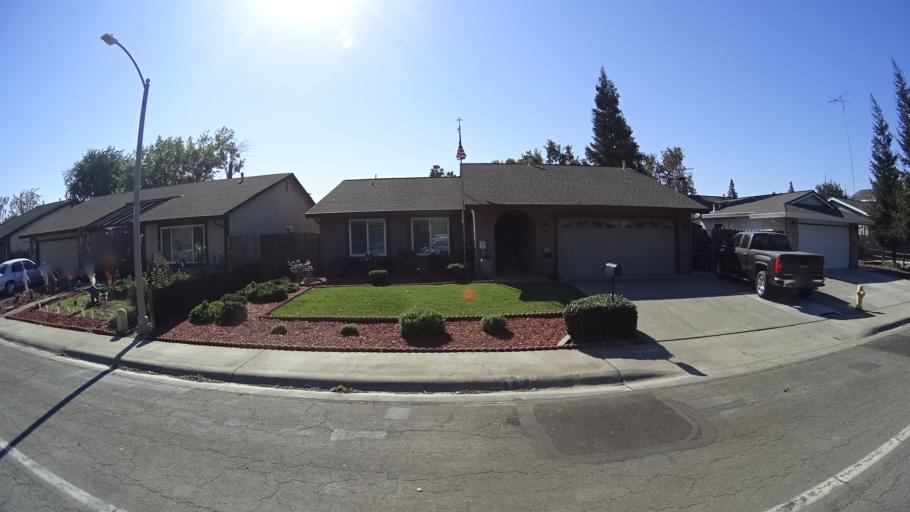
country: US
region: California
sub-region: Yolo County
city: Woodland
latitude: 38.6631
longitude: -121.8002
